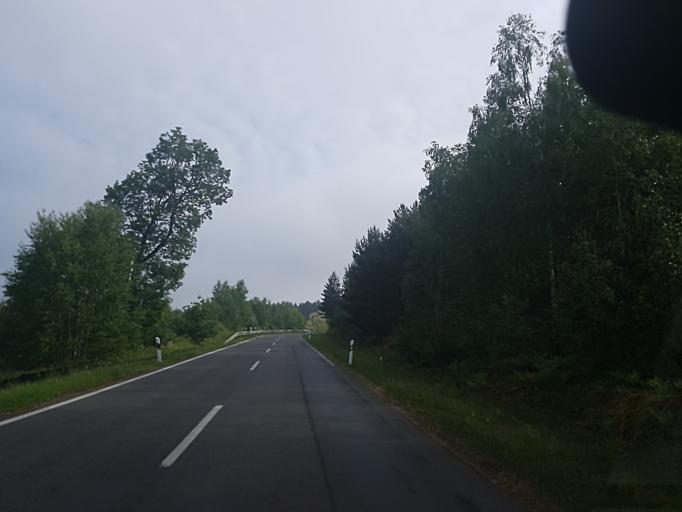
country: DE
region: Brandenburg
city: Gorzke
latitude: 52.0931
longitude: 12.3351
